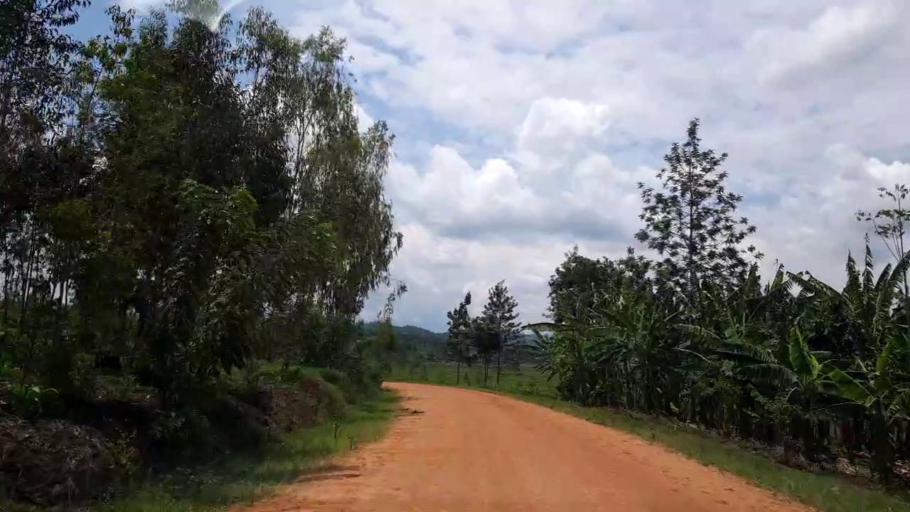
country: RW
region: Northern Province
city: Byumba
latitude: -1.5680
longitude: 30.2988
